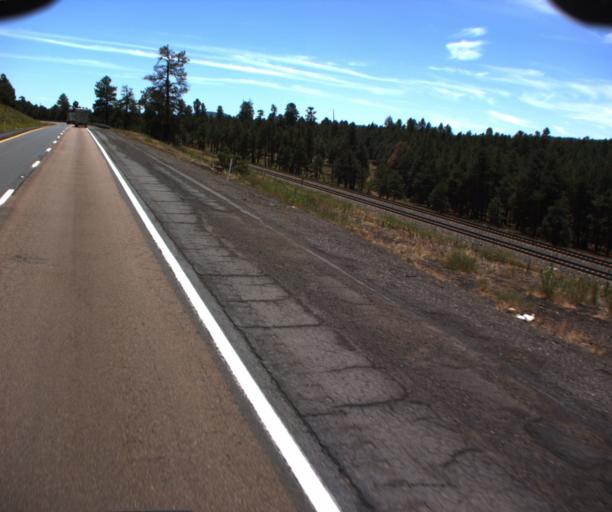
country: US
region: Arizona
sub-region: Coconino County
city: Flagstaff
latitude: 35.2089
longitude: -111.7721
